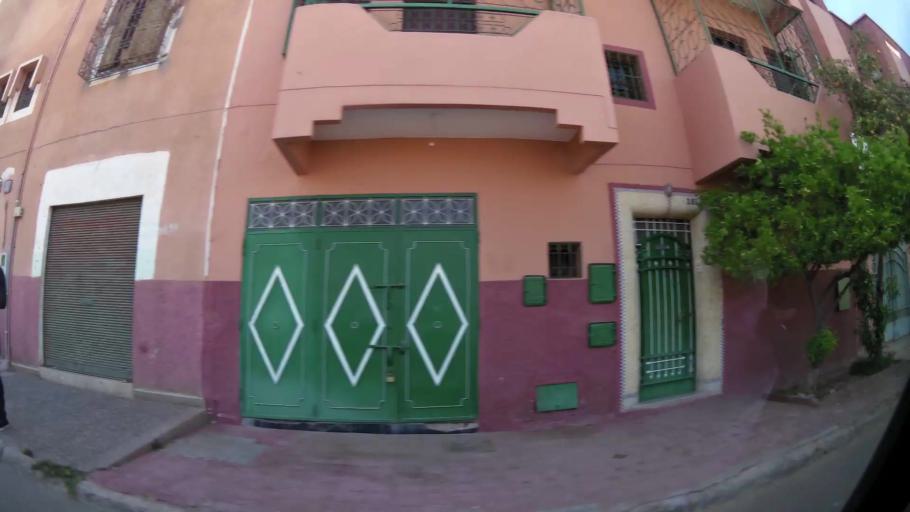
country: MA
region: Marrakech-Tensift-Al Haouz
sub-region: Marrakech
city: Marrakesh
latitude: 31.6584
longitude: -8.0121
